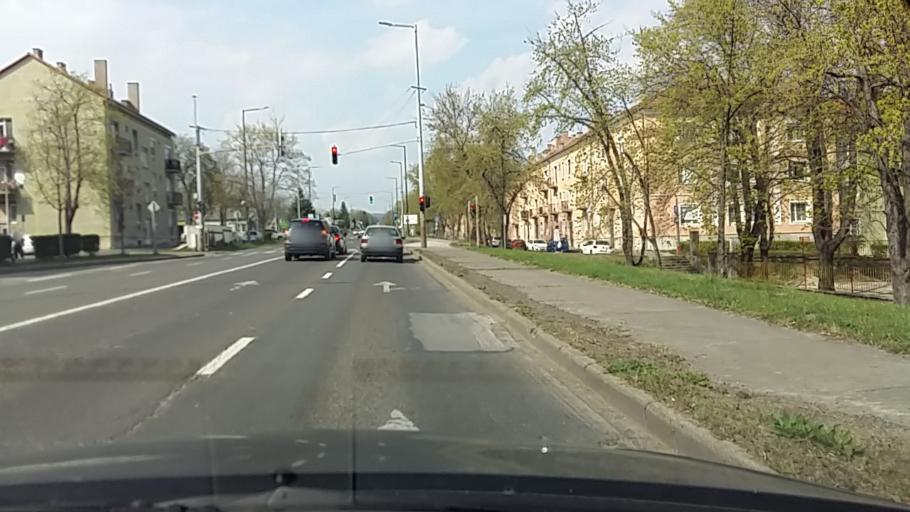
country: HU
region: Baranya
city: Pecs
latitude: 46.0919
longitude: 18.2687
